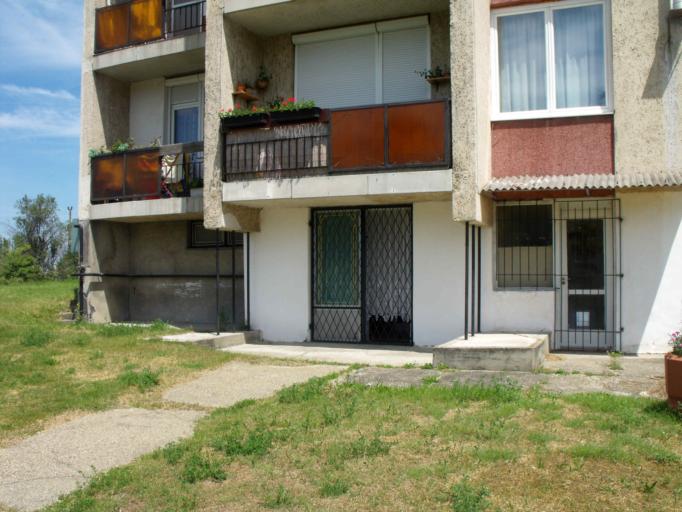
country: HU
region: Komarom-Esztergom
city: Labatlan
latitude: 47.7475
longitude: 18.4952
